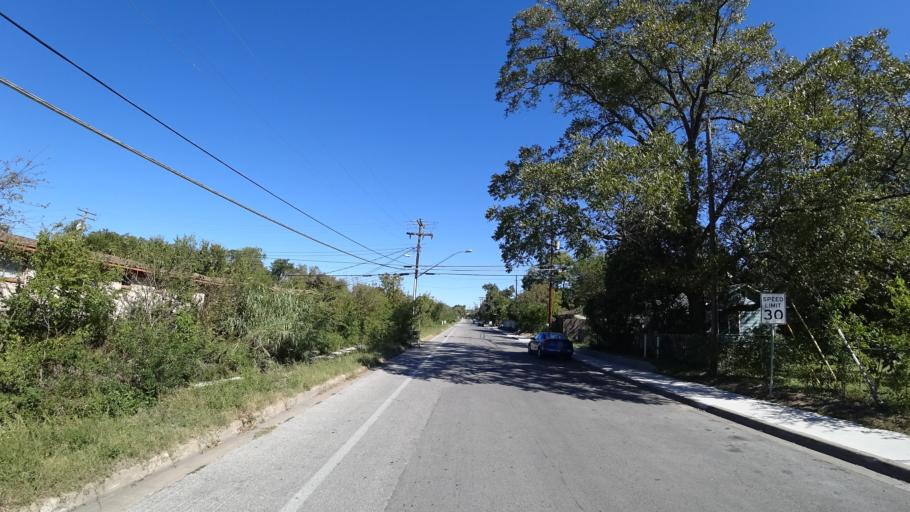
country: US
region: Texas
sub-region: Travis County
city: Austin
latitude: 30.3190
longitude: -97.7243
